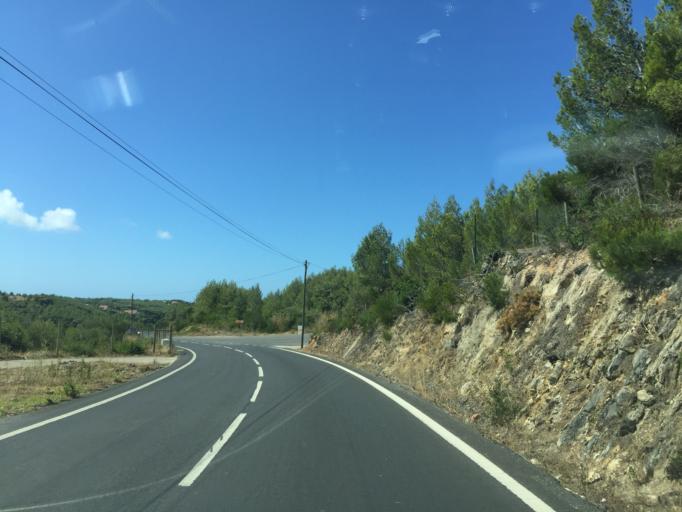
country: PT
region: Lisbon
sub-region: Cascais
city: Alcabideche
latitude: 38.7438
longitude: -9.4535
